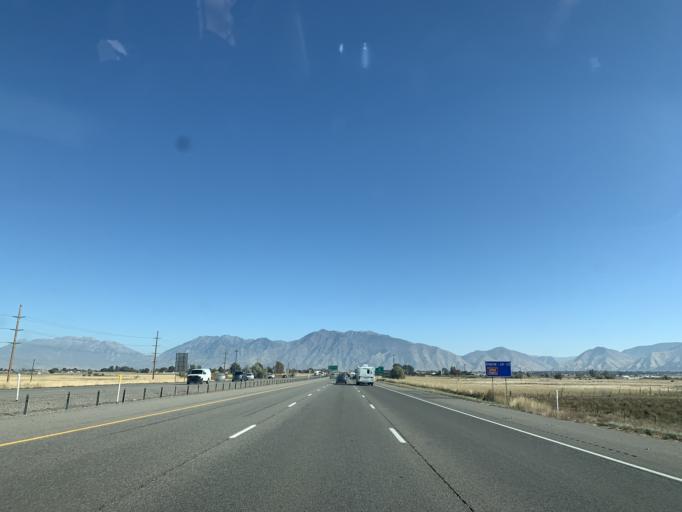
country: US
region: Utah
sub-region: Utah County
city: Payson
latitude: 40.0687
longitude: -111.7196
